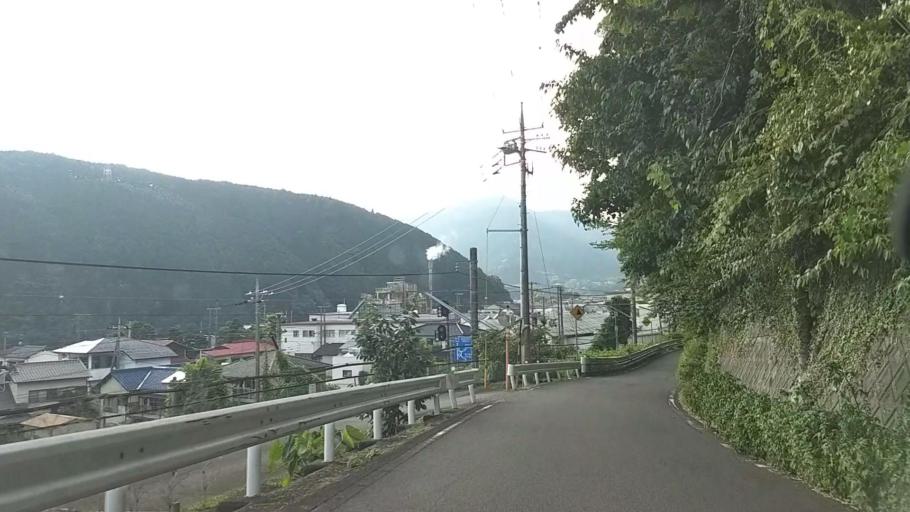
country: JP
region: Shizuoka
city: Fujinomiya
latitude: 35.1952
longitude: 138.5658
